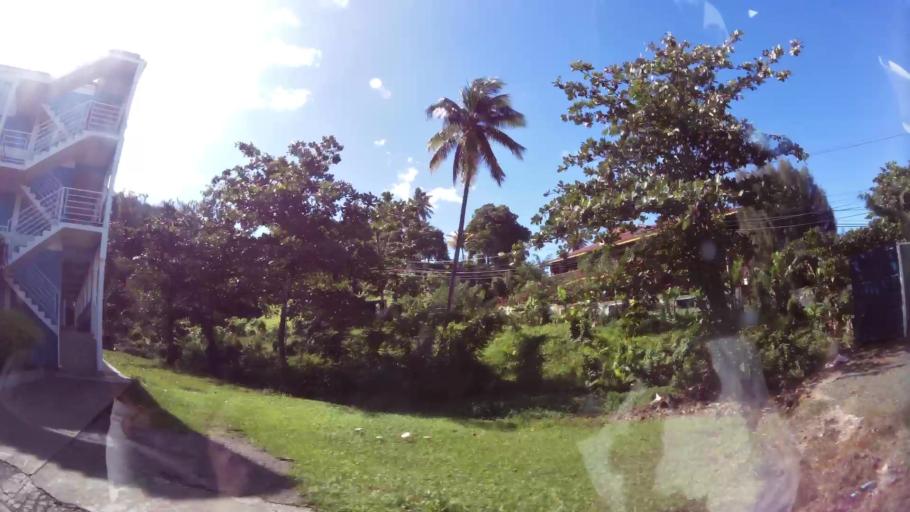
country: DM
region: Saint John
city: Portsmouth
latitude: 15.5528
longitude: -61.4578
